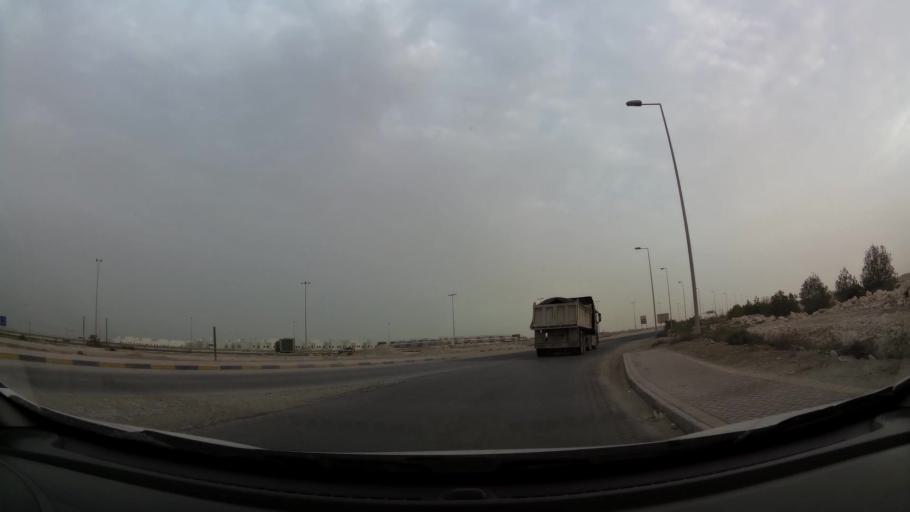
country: BH
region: Northern
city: Ar Rifa'
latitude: 26.0450
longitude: 50.6066
